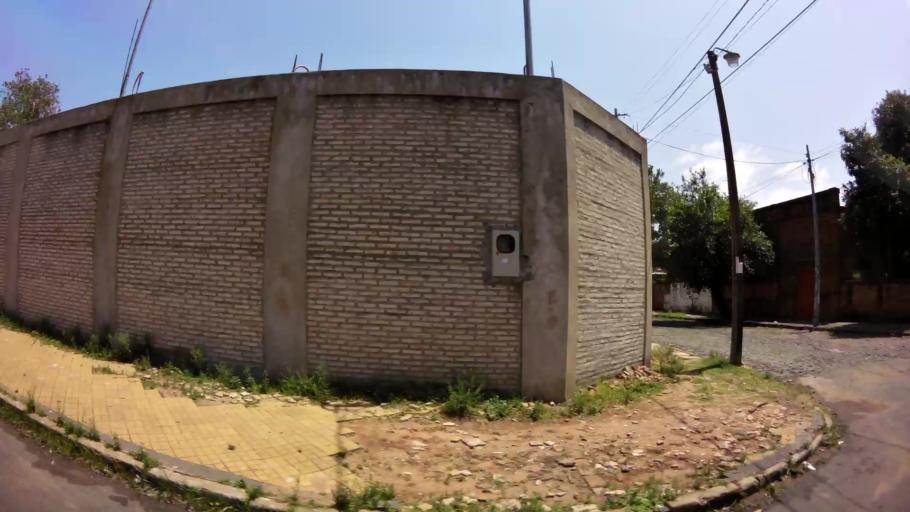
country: PY
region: Asuncion
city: Asuncion
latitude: -25.2974
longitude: -57.6427
